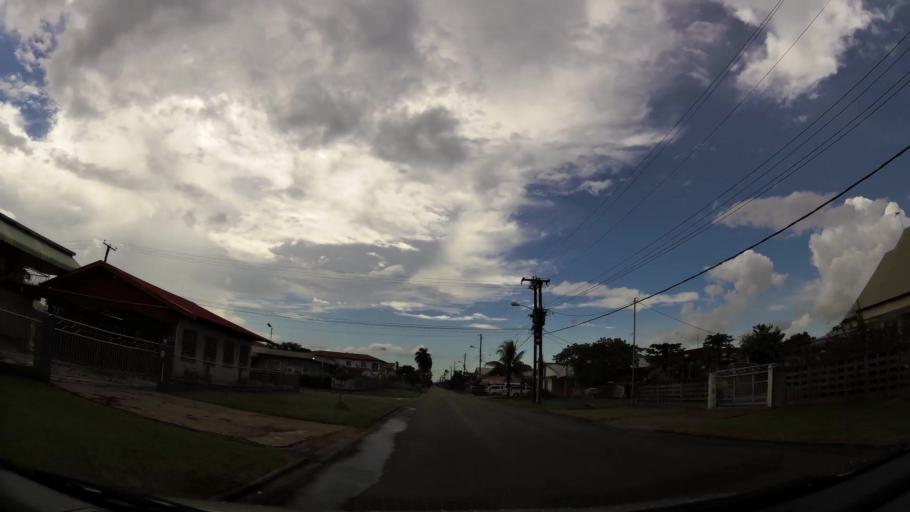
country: SR
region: Paramaribo
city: Paramaribo
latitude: 5.8420
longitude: -55.1230
